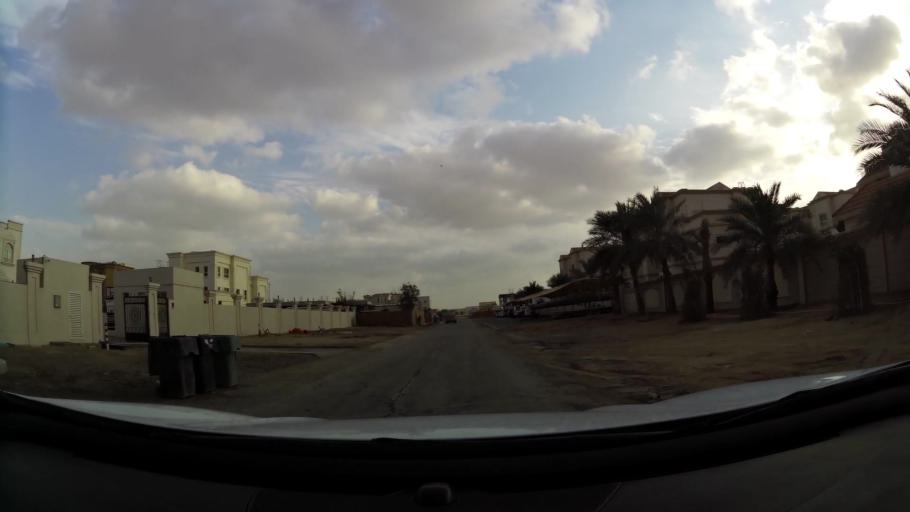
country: AE
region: Abu Dhabi
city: Abu Dhabi
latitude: 24.3535
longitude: 54.5618
